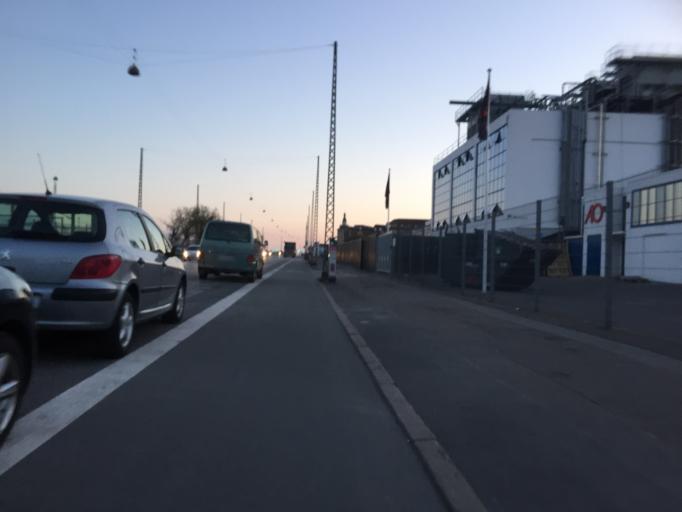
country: DK
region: Capital Region
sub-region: Kobenhavn
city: Copenhagen
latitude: 55.6668
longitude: 12.5620
